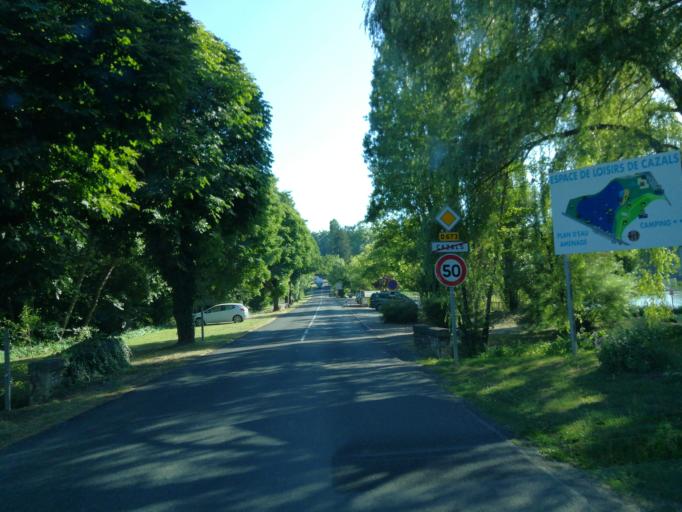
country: FR
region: Midi-Pyrenees
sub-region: Departement du Lot
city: Salviac
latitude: 44.6419
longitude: 1.2217
